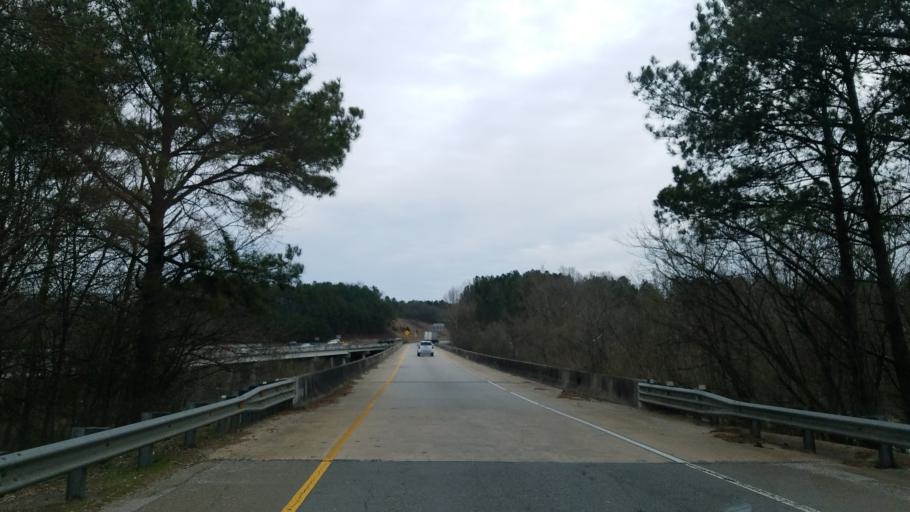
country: US
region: Georgia
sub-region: Cherokee County
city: Canton
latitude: 34.2521
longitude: -84.4684
